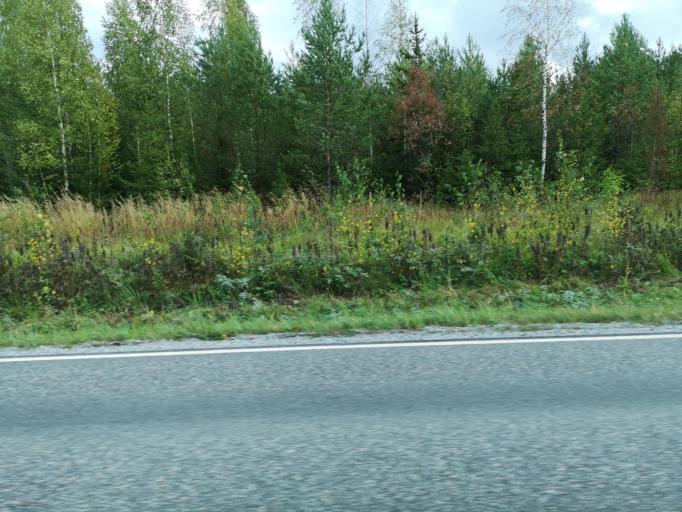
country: FI
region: Central Finland
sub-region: Jyvaeskylae
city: Hankasalmi
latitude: 62.3560
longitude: 26.4539
